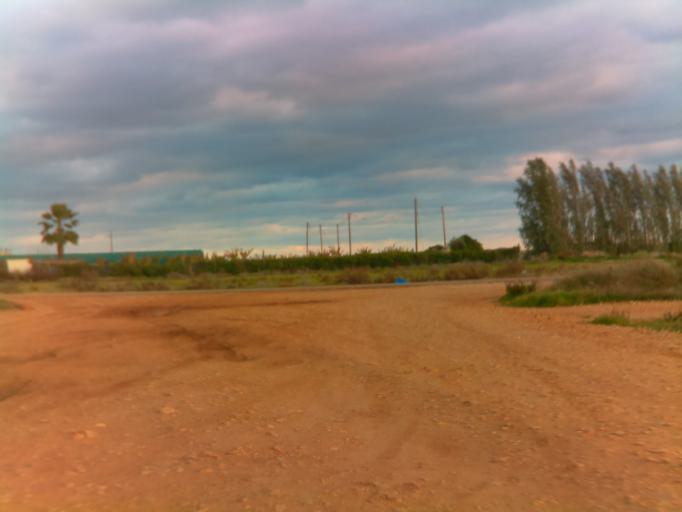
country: CY
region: Pafos
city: Pegeia
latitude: 34.8727
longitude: 32.3422
